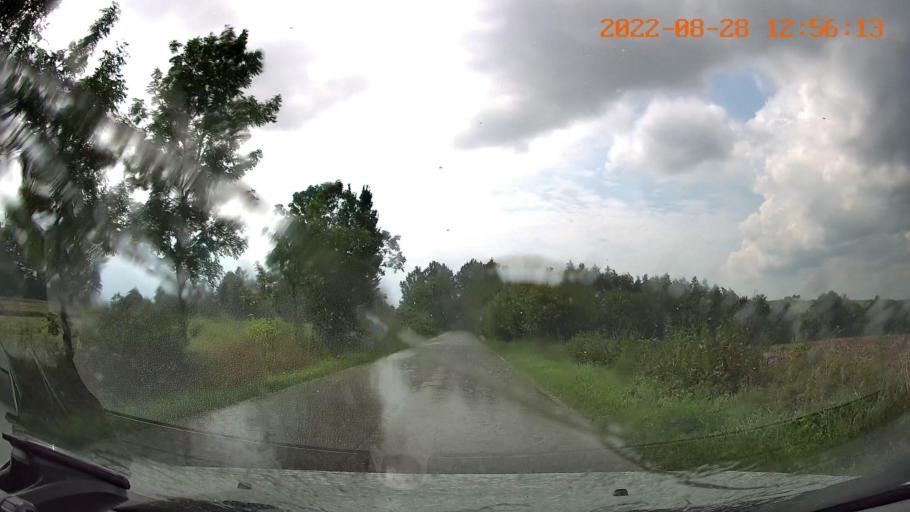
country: PL
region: Swietokrzyskie
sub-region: Powiat jedrzejowski
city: Wodzislaw
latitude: 50.3675
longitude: 20.1961
